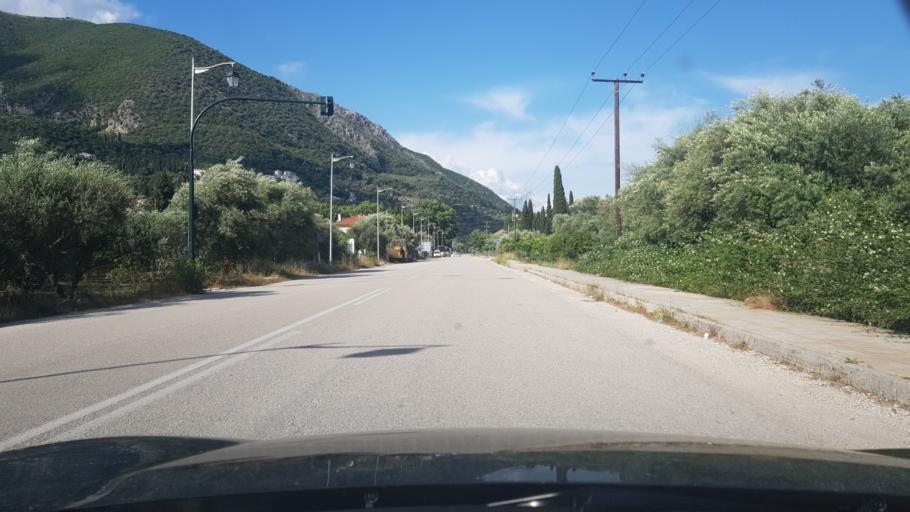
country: GR
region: Ionian Islands
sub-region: Lefkada
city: Nidri
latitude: 38.7104
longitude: 20.7063
